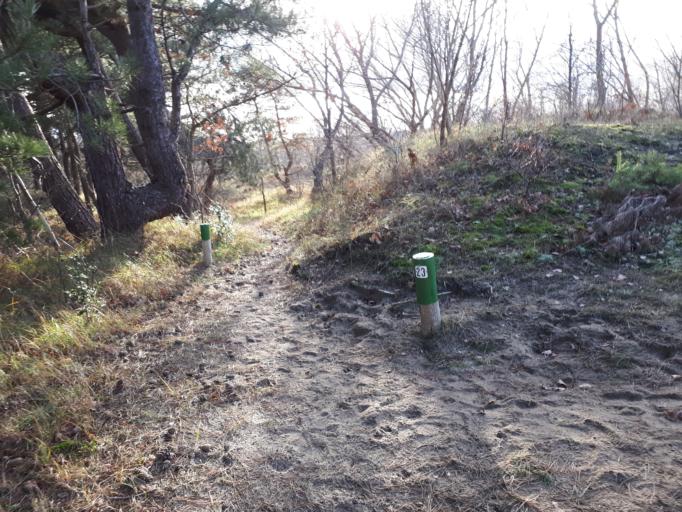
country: NL
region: South Holland
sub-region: Gemeente Wassenaar
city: Wassenaar
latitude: 52.1483
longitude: 4.3705
